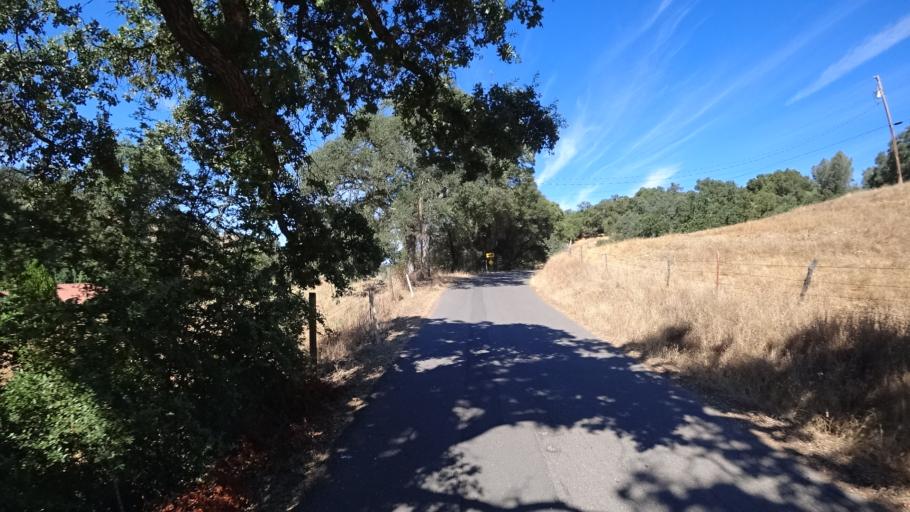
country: US
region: California
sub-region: Calaveras County
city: Angels Camp
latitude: 38.1461
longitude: -120.5910
